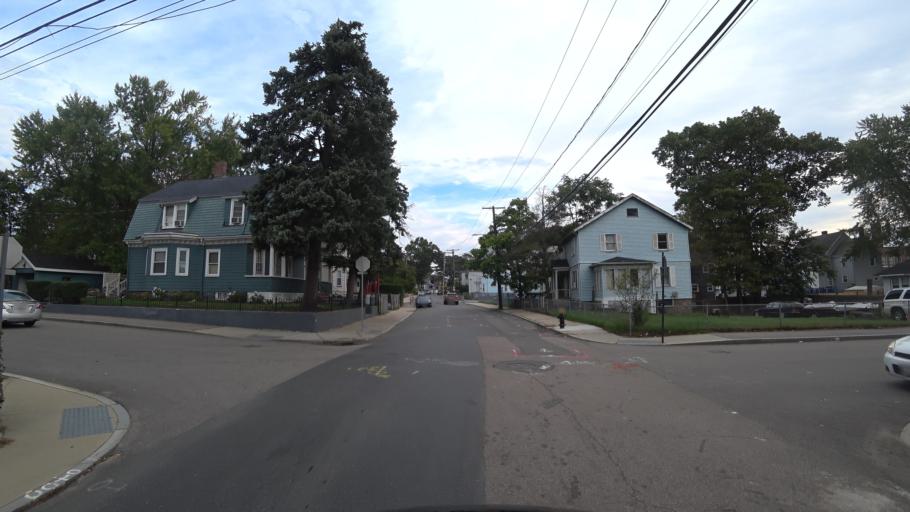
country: US
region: Massachusetts
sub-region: Norfolk County
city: Milton
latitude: 42.2672
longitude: -71.1063
